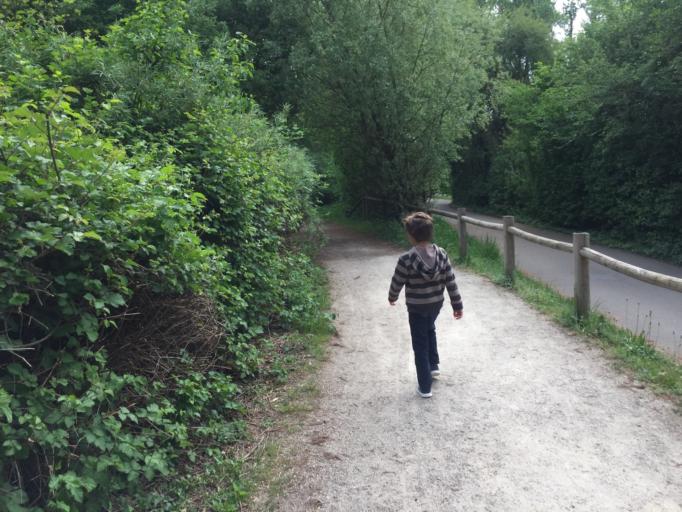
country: FR
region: Rhone-Alpes
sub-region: Departement du Rhone
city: Vaulx-en-Velin
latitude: 45.7982
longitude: 4.9385
